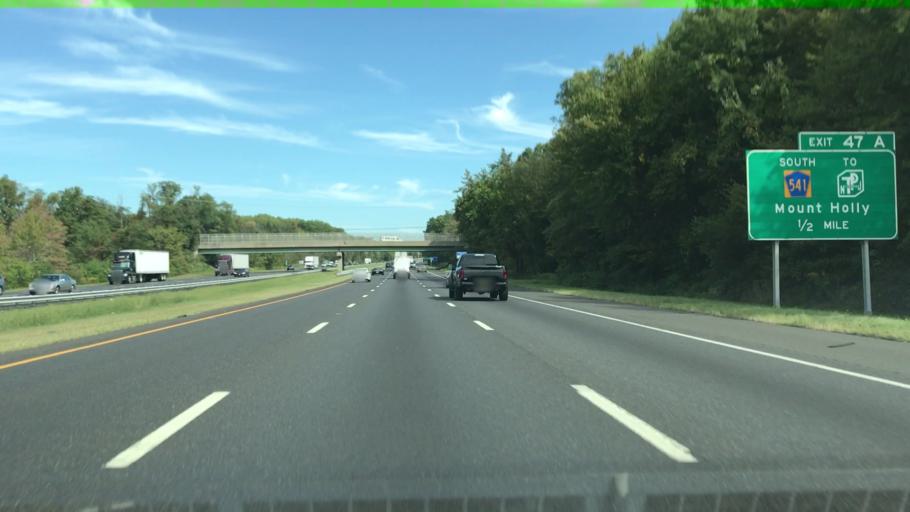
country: US
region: New Jersey
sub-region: Burlington County
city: Willingboro
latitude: 40.0352
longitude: -74.8393
